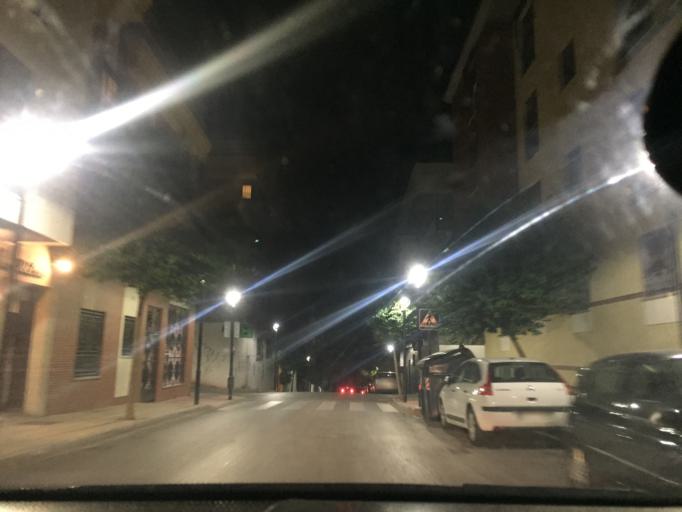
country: ES
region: Andalusia
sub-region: Provincia de Jaen
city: Jaen
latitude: 37.7712
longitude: -3.7827
